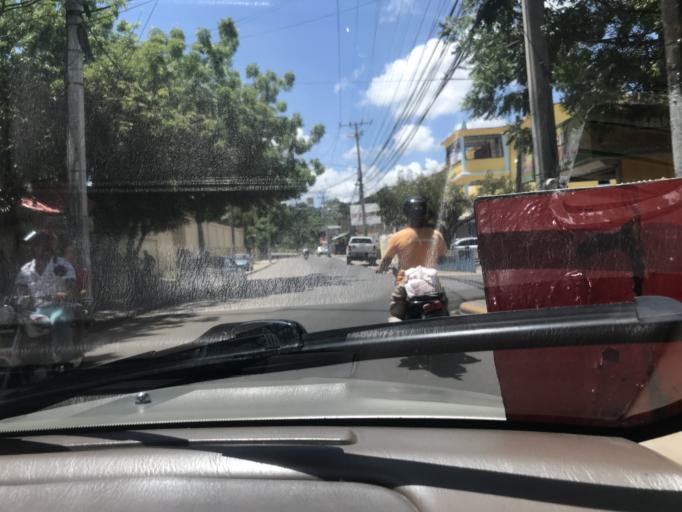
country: DO
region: Santiago
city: Santiago de los Caballeros
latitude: 19.4191
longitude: -70.6893
